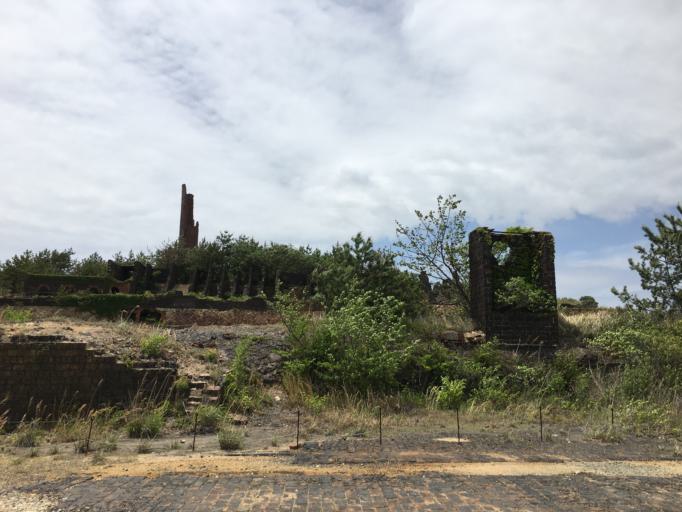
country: JP
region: Kagawa
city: Tonosho
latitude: 34.5634
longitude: 134.1068
